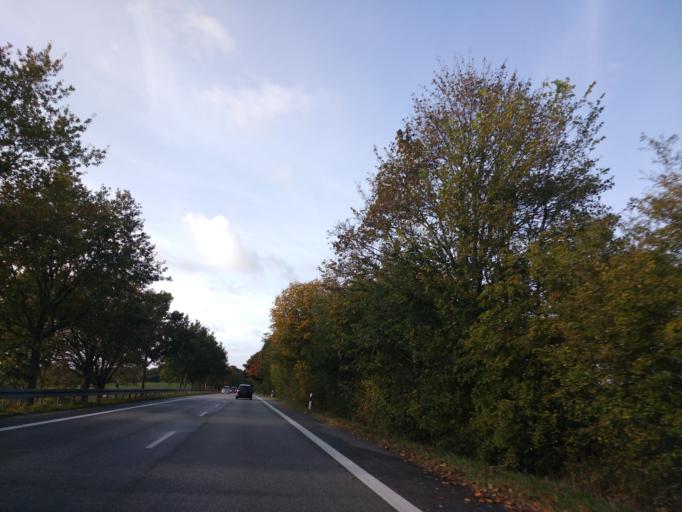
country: DE
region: Schleswig-Holstein
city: Schashagen
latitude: 54.1293
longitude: 10.8983
